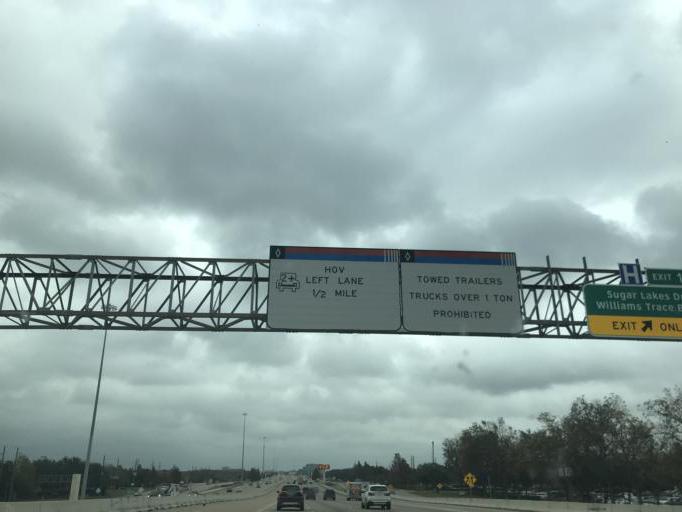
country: US
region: Texas
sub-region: Fort Bend County
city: Sugar Land
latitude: 29.5992
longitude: -95.6215
